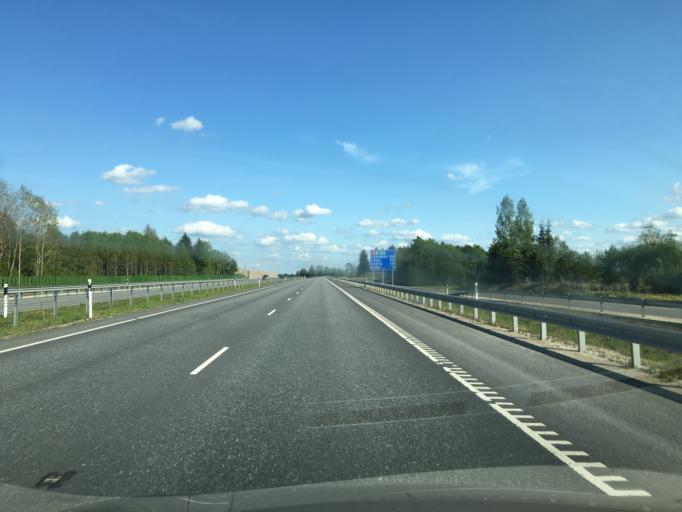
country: EE
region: Harju
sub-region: Rae vald
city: Vaida
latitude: 59.1861
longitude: 25.0667
